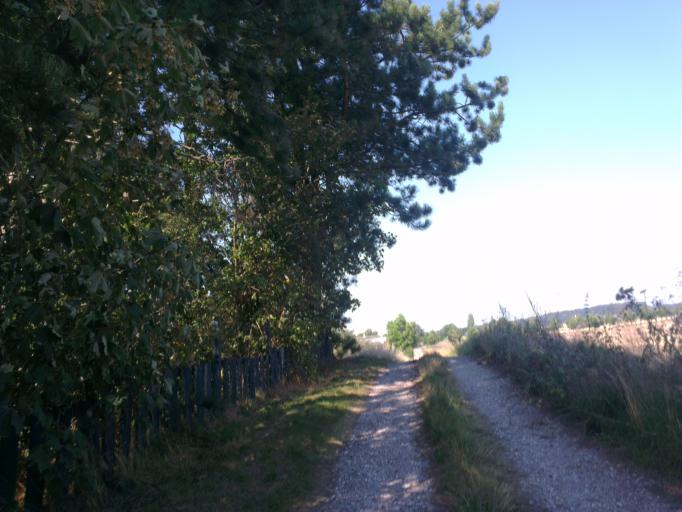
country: DK
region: Capital Region
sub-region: Frederikssund Kommune
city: Skibby
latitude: 55.7644
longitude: 11.9460
